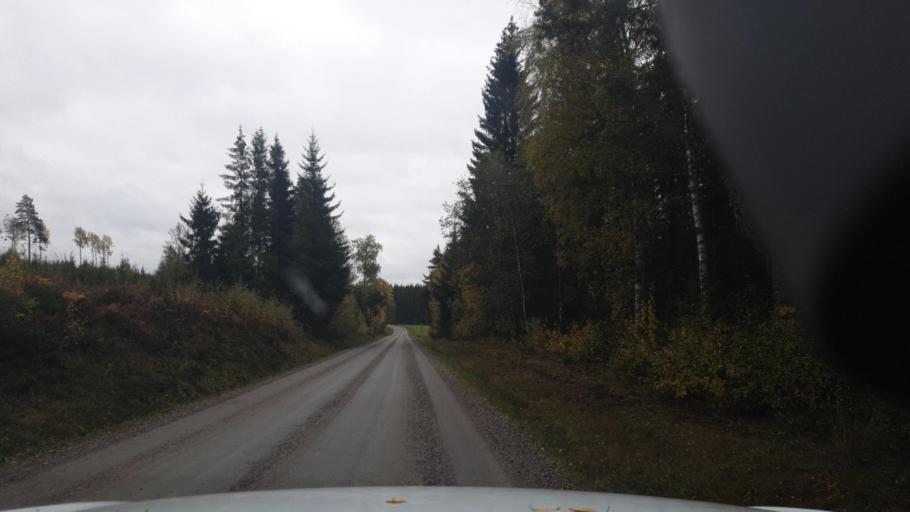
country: SE
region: Vaermland
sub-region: Karlstads Kommun
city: Edsvalla
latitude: 59.4920
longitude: 13.0309
